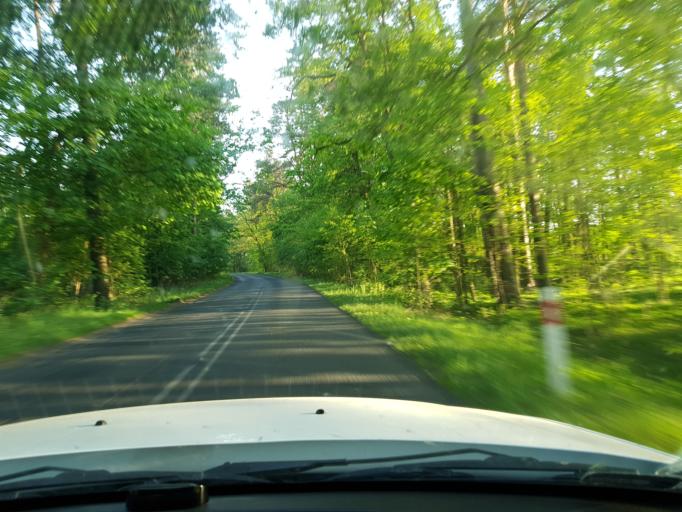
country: PL
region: West Pomeranian Voivodeship
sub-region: Powiat stargardzki
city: Kobylanka
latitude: 53.4382
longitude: 14.9096
